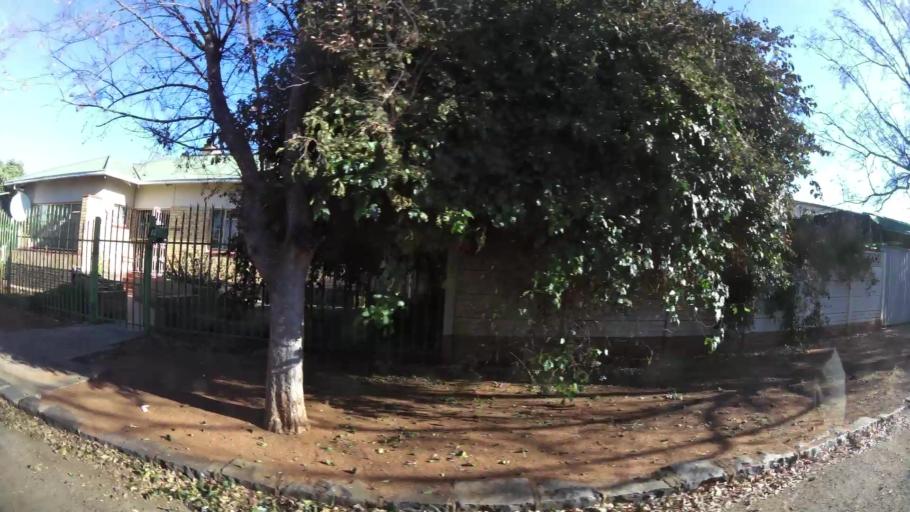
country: ZA
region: Northern Cape
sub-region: Frances Baard District Municipality
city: Kimberley
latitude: -28.7522
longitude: 24.7834
